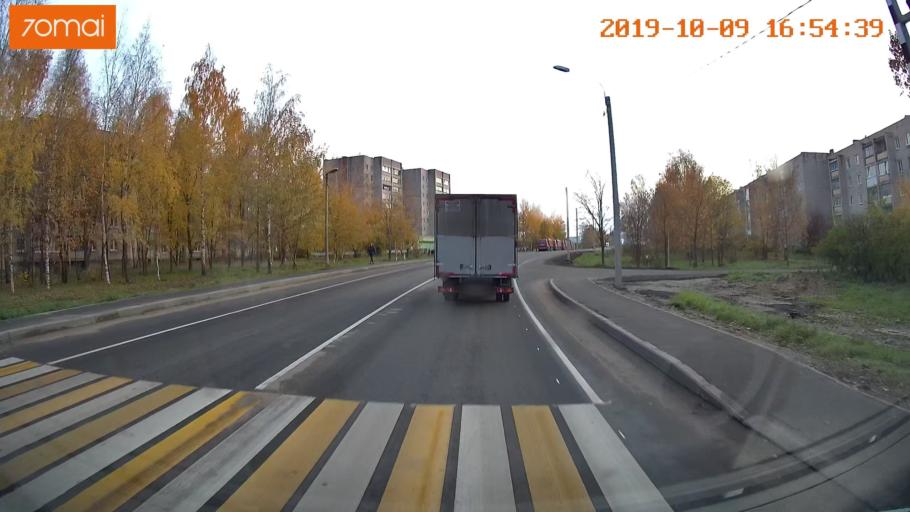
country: RU
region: Ivanovo
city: Privolzhsk
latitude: 57.3723
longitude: 41.2786
